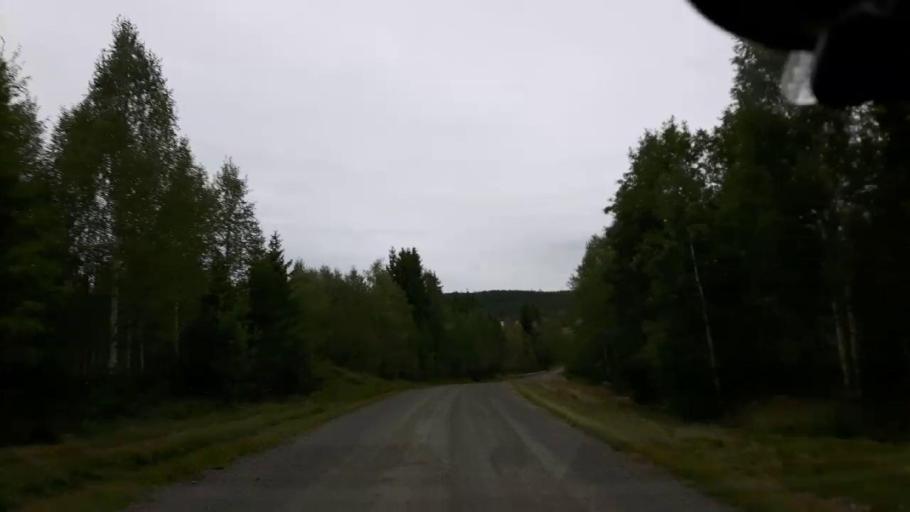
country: SE
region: Vaesternorrland
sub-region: Ange Kommun
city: Fransta
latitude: 62.8638
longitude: 15.9847
